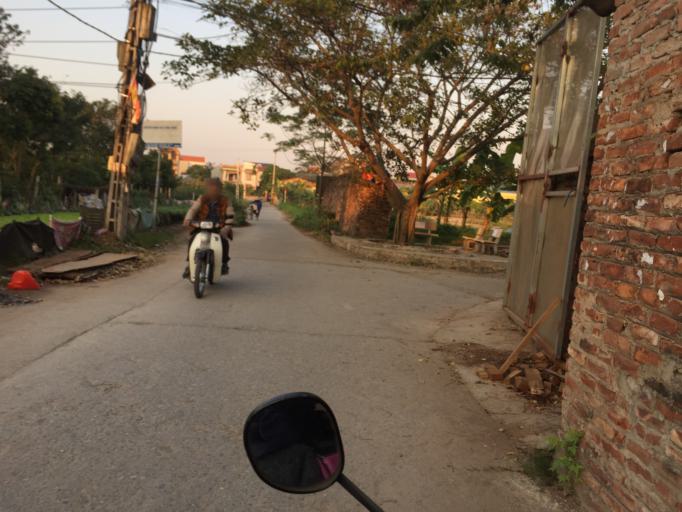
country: VN
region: Ha Noi
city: Chuc Son
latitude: 20.9114
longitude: 105.7309
